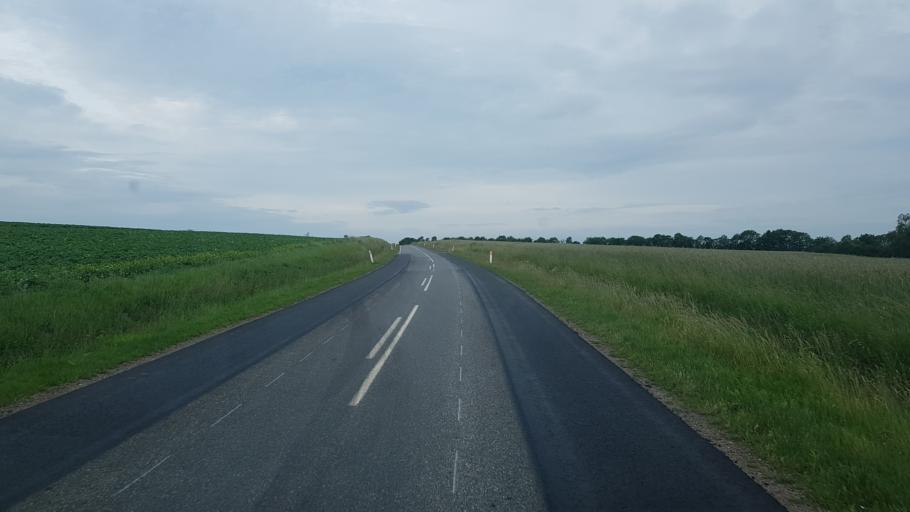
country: DK
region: South Denmark
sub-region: Vejen Kommune
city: Holsted
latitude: 55.4414
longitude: 8.9485
